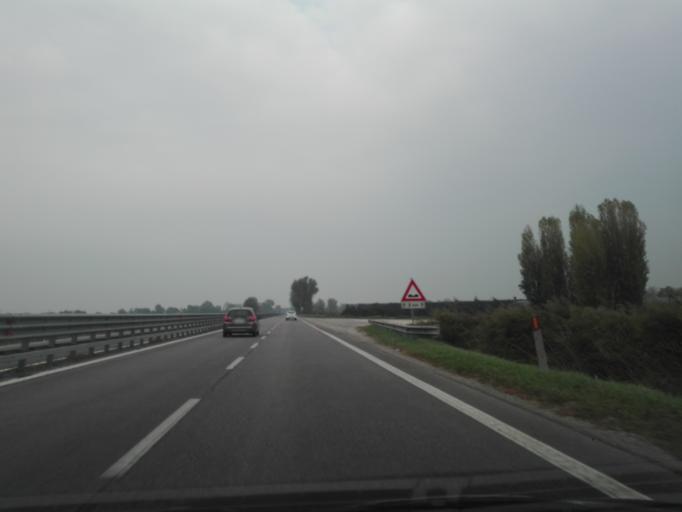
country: IT
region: Veneto
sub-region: Provincia di Verona
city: Villa Bartolomea
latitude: 45.1565
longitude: 11.3210
